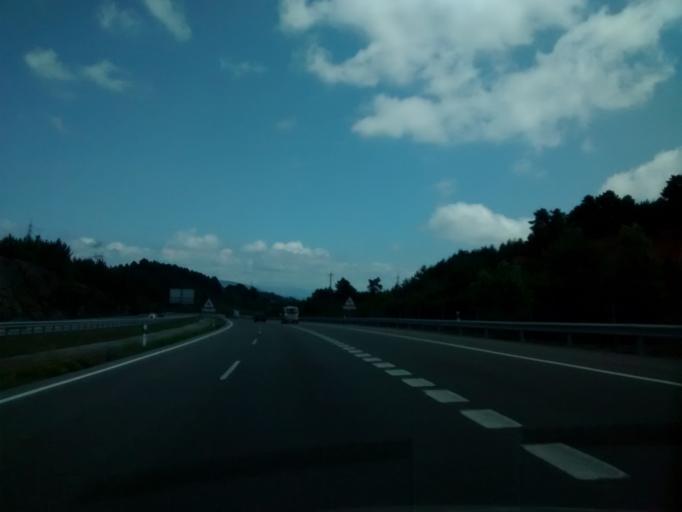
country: ES
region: Castille and Leon
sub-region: Provincia de Leon
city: Molinaseca
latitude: 42.5637
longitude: -6.5512
